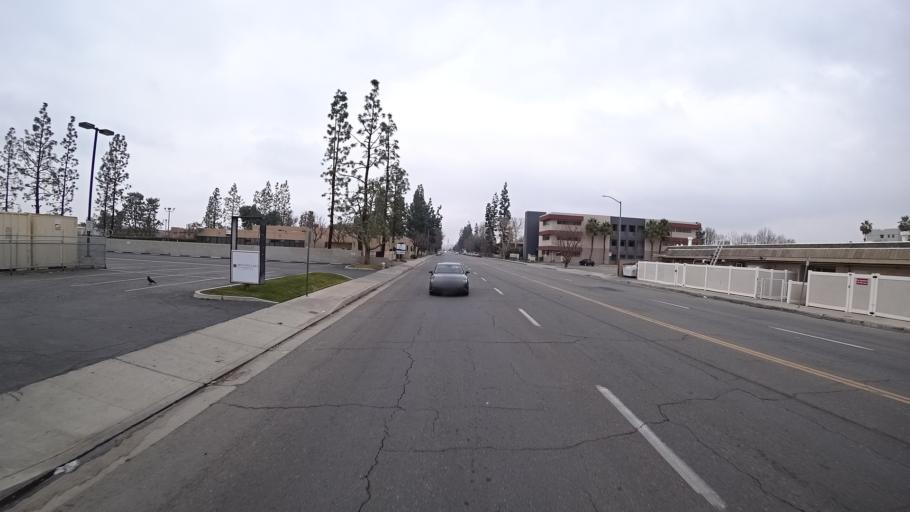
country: US
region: California
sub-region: Kern County
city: Bakersfield
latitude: 35.3912
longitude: -119.0106
